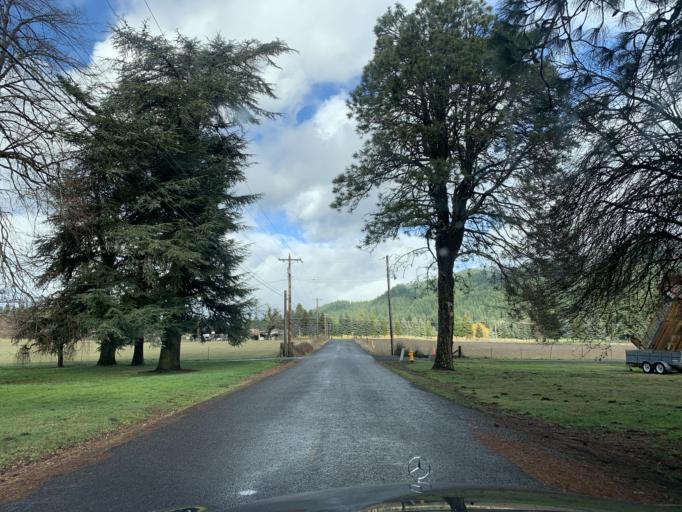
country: US
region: Washington
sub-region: Skamania County
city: Carson
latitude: 45.7237
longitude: -121.8047
